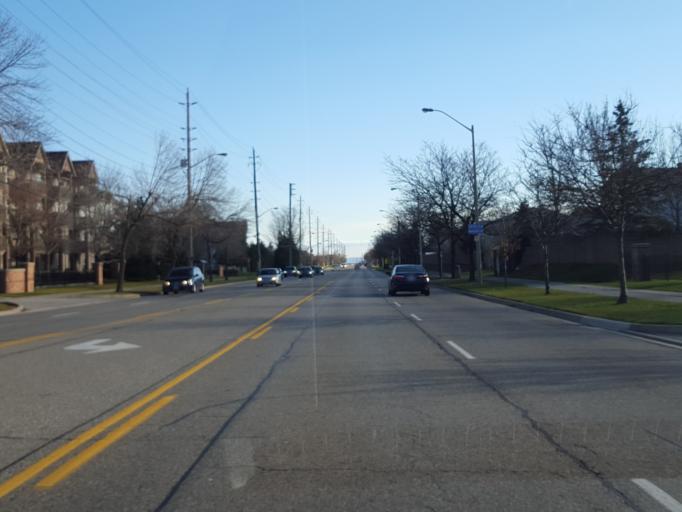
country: CA
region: Ontario
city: Burlington
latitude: 43.3782
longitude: -79.8045
